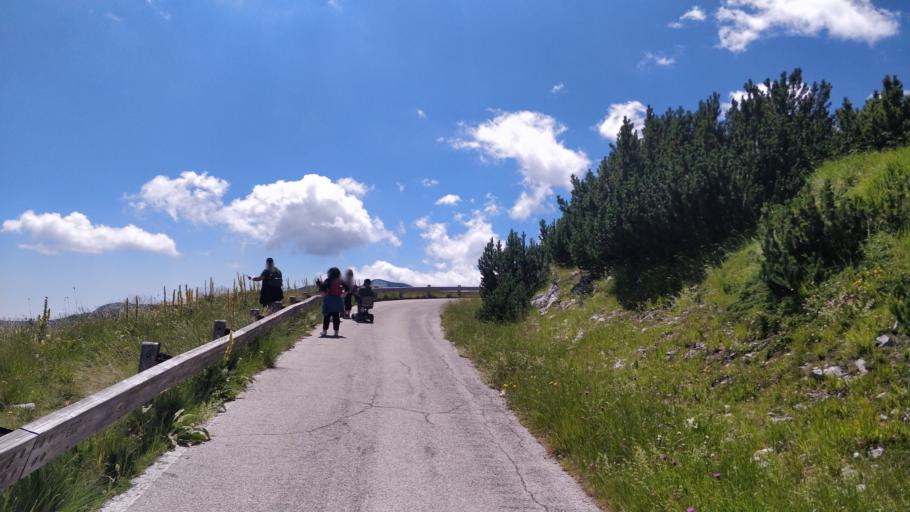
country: IT
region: Abruzzo
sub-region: Provincia di Chieti
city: Pretoro
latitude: 42.1588
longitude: 14.1331
